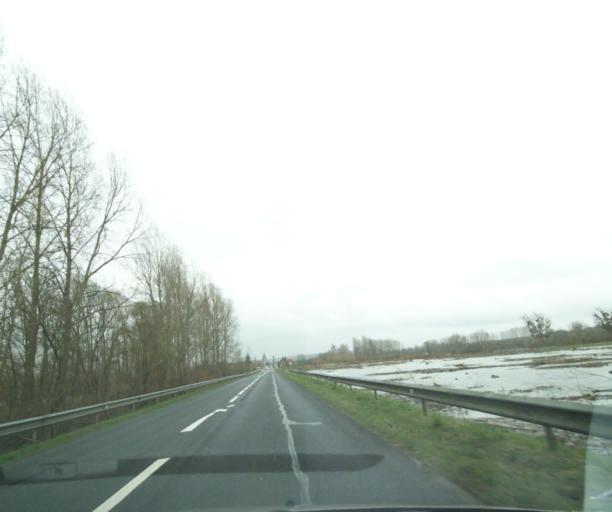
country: FR
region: Picardie
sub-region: Departement de l'Oise
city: Carlepont
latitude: 49.5572
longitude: 3.0411
